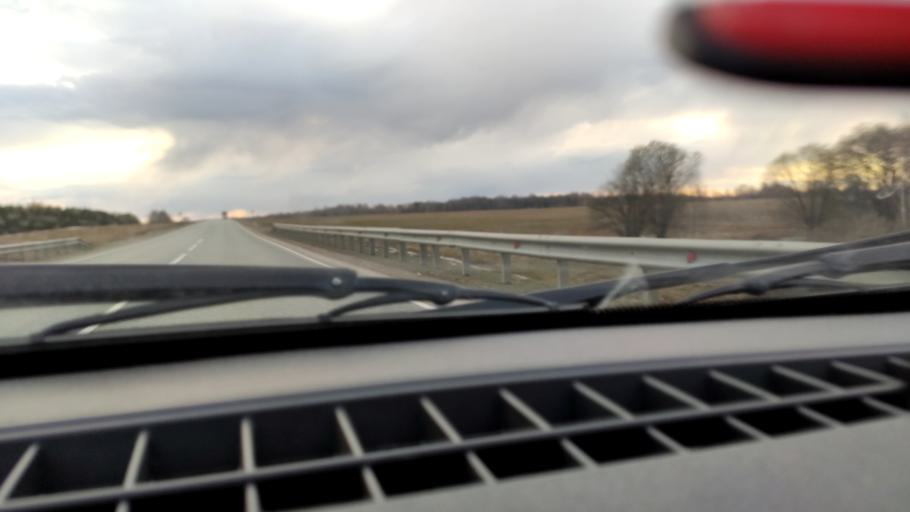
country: RU
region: Bashkortostan
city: Kudeyevskiy
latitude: 54.8167
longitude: 56.7272
